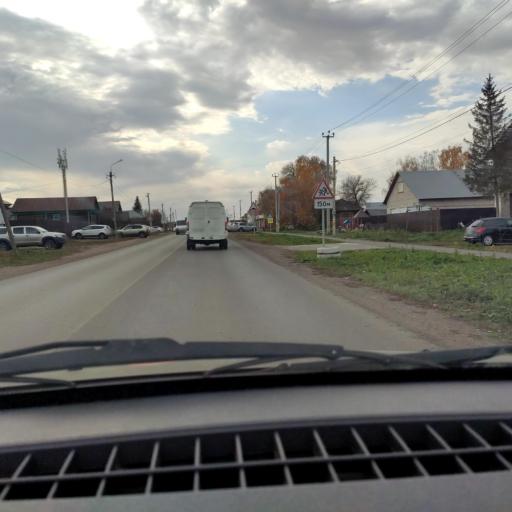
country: RU
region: Bashkortostan
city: Ufa
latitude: 54.6165
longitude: 55.9035
